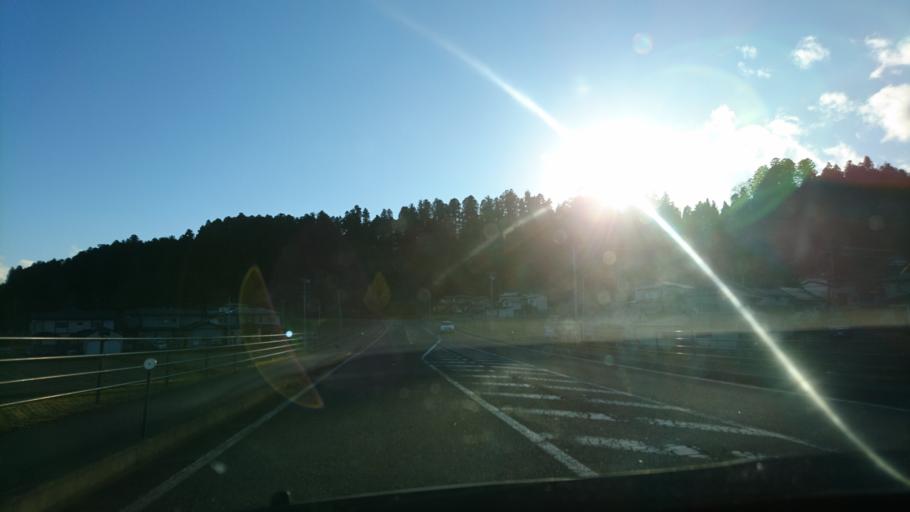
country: JP
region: Iwate
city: Ichinoseki
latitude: 39.0032
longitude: 141.1071
